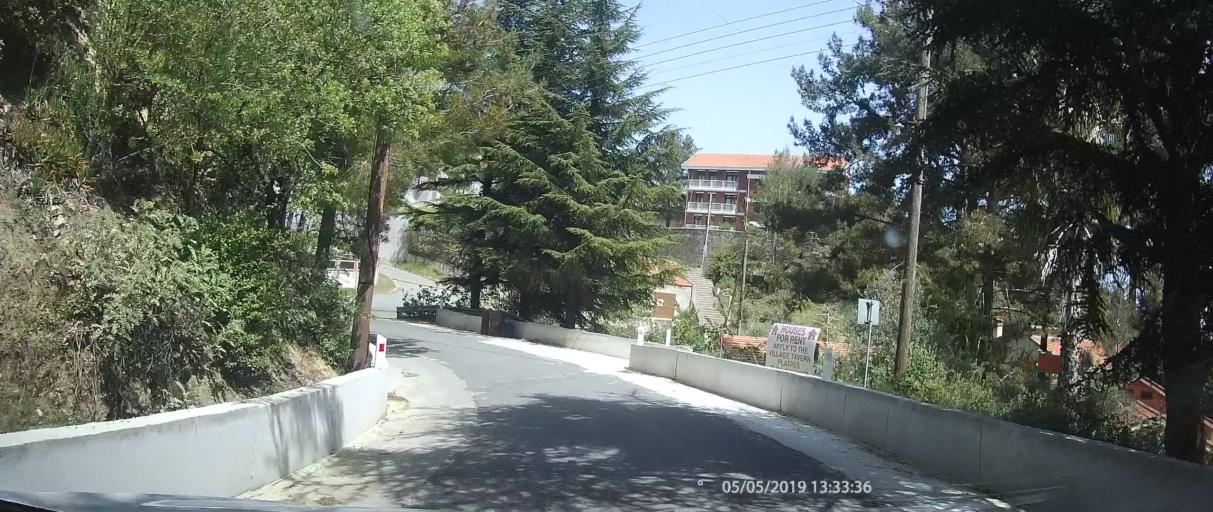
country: CY
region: Limassol
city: Pelendri
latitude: 34.8852
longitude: 32.8575
